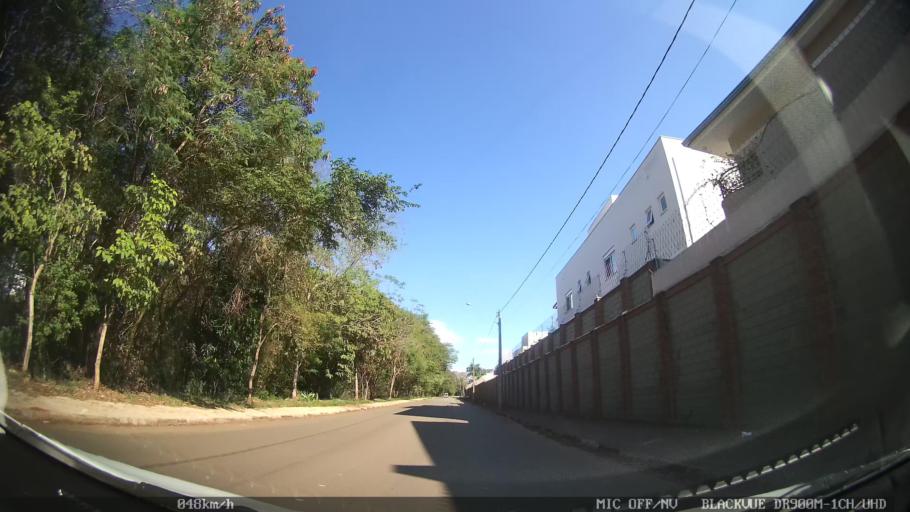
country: BR
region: Sao Paulo
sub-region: Sumare
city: Sumare
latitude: -22.8215
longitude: -47.2814
